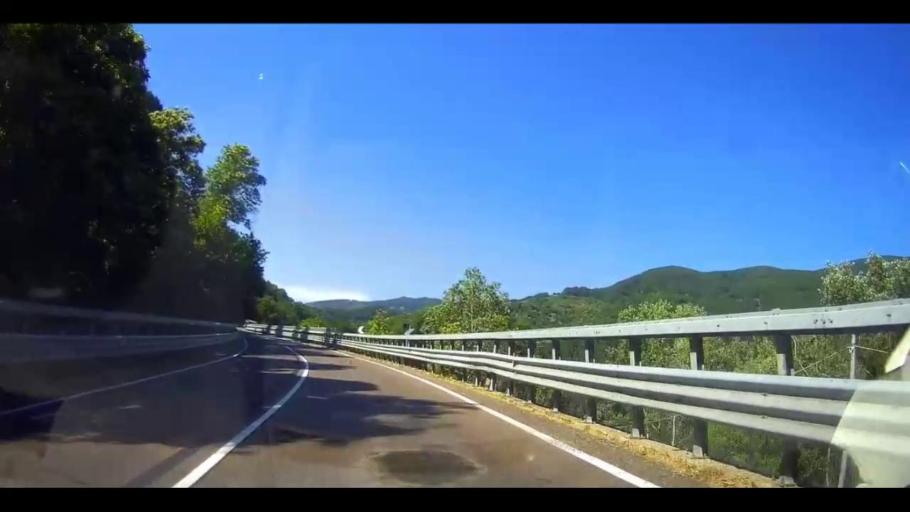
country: IT
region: Calabria
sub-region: Provincia di Cosenza
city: Spezzano Piccolo
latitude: 39.2930
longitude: 16.3510
